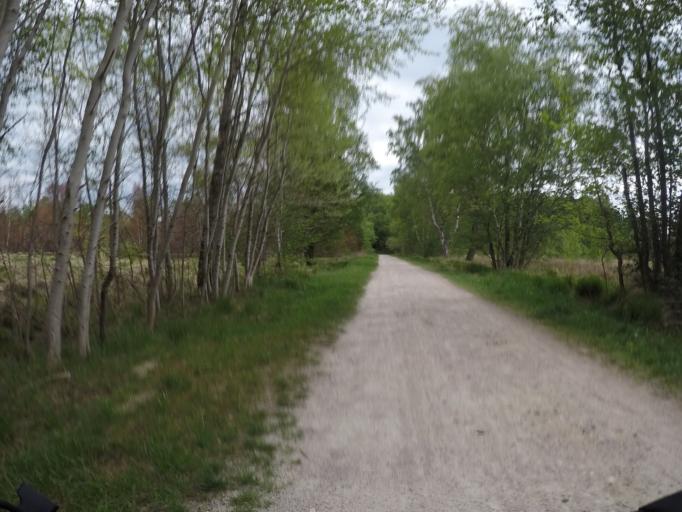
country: DE
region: Schleswig-Holstein
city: Henstedt-Ulzburg
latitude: 53.7547
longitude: 10.0156
